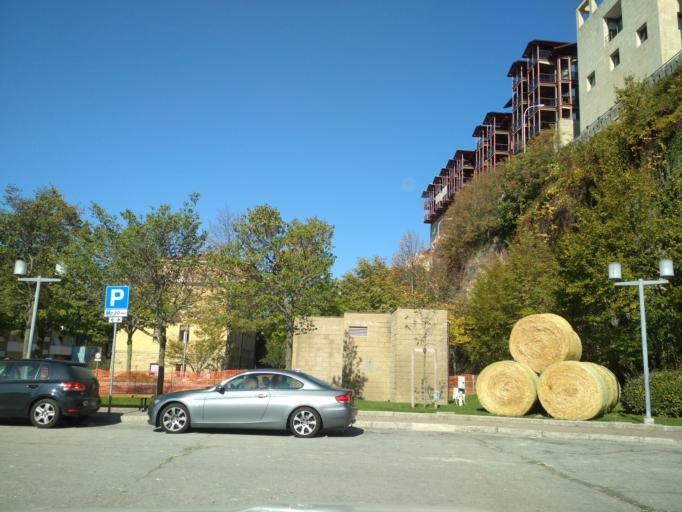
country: SM
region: San Marino
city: San Marino
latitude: 43.9351
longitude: 12.4460
